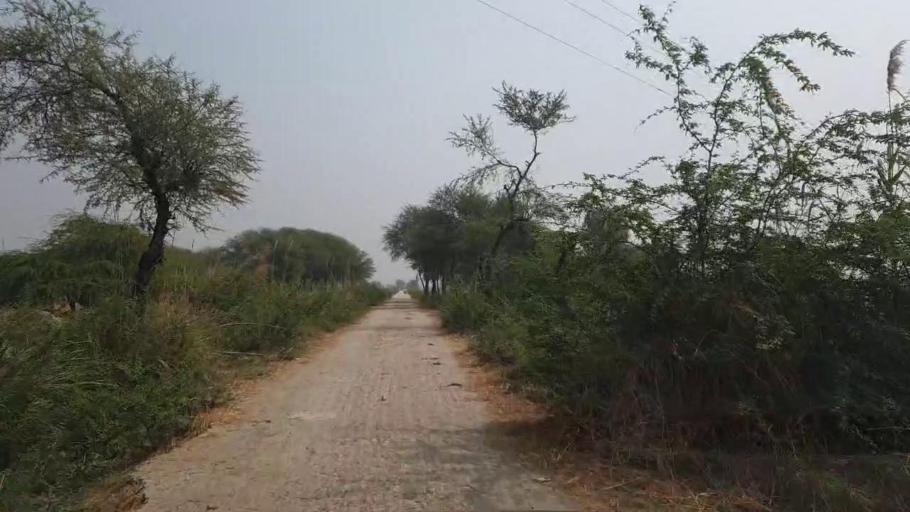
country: PK
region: Sindh
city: Kario
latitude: 24.6524
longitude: 68.6050
